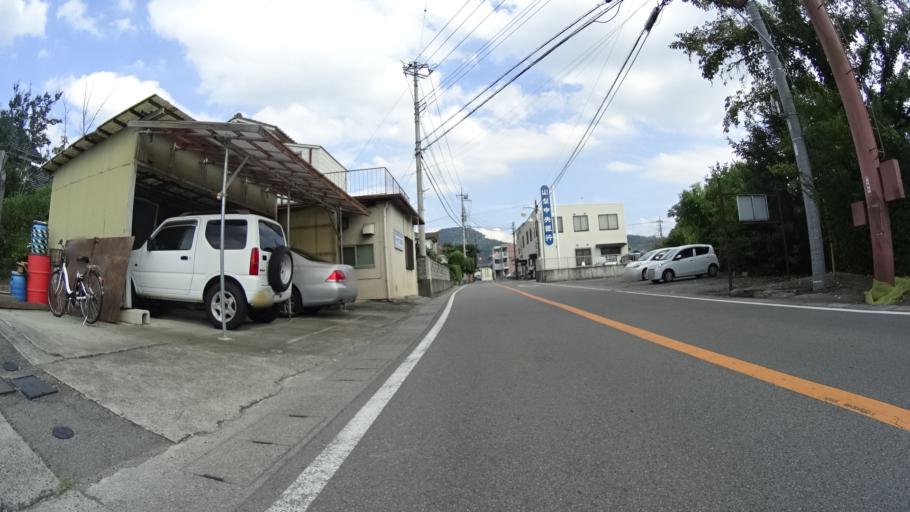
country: JP
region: Yamanashi
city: Kofu-shi
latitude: 35.6823
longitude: 138.5676
